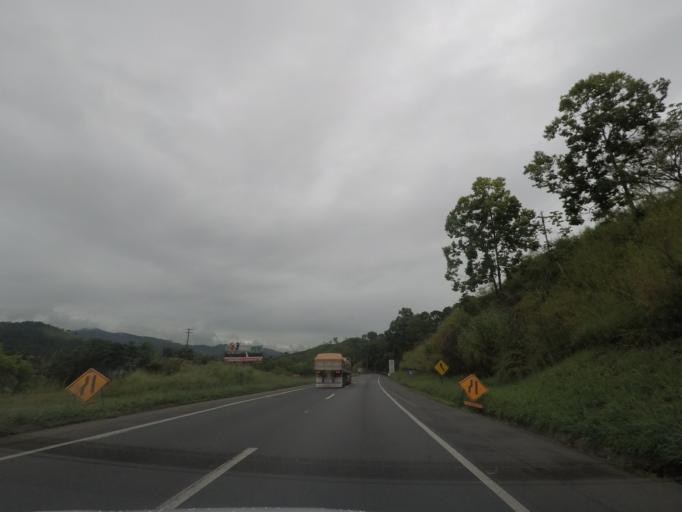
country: BR
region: Sao Paulo
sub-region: Cajati
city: Cajati
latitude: -24.8257
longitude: -48.2092
